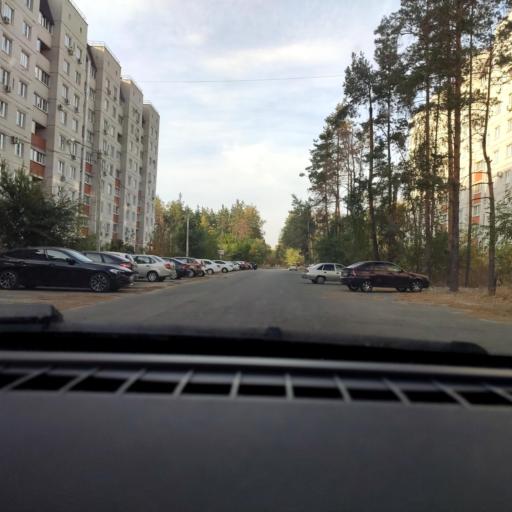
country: RU
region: Voronezj
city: Voronezh
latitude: 51.6933
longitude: 39.2800
